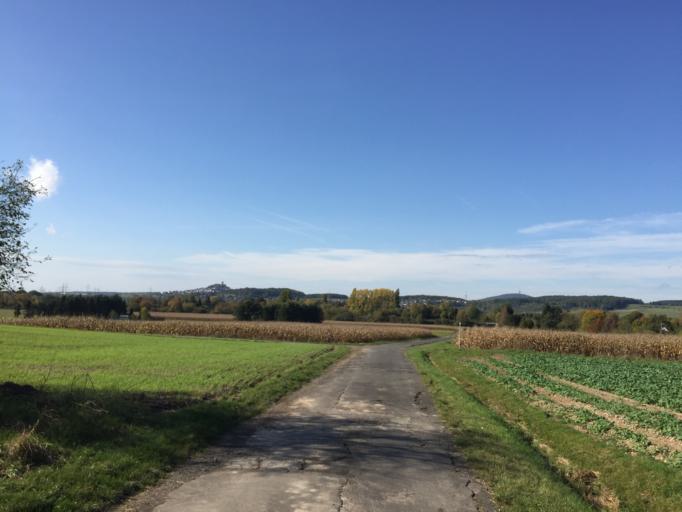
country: DE
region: Hesse
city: Lollar
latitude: 50.6171
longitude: 8.6931
